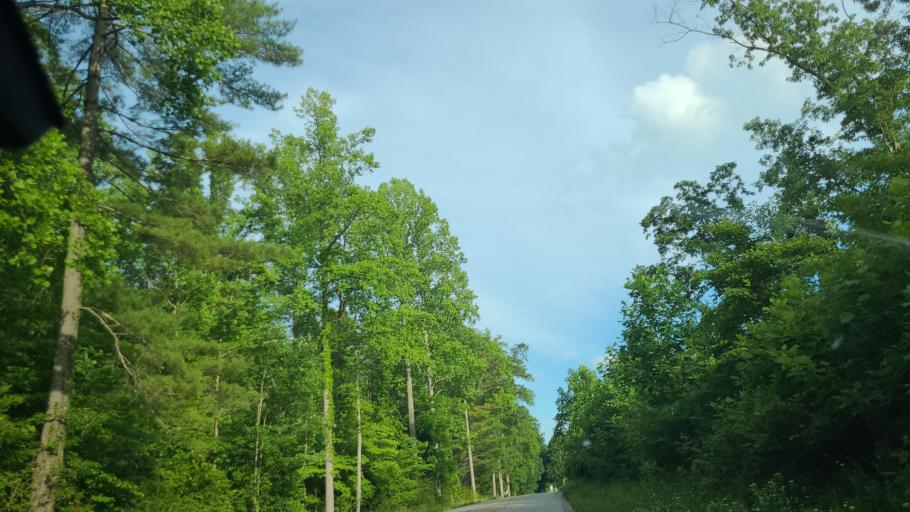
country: US
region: Kentucky
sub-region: Whitley County
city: Corbin
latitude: 36.9110
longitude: -84.2473
